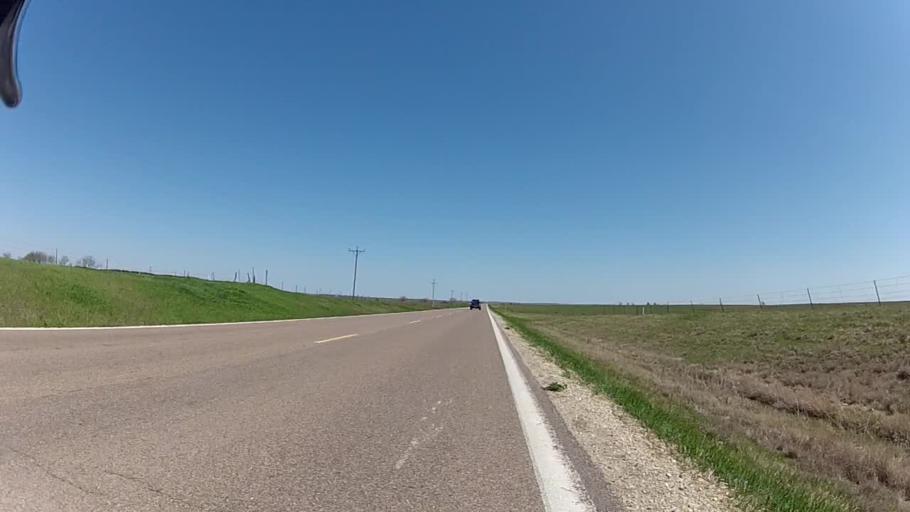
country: US
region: Kansas
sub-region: Morris County
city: Council Grove
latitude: 38.8876
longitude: -96.5202
